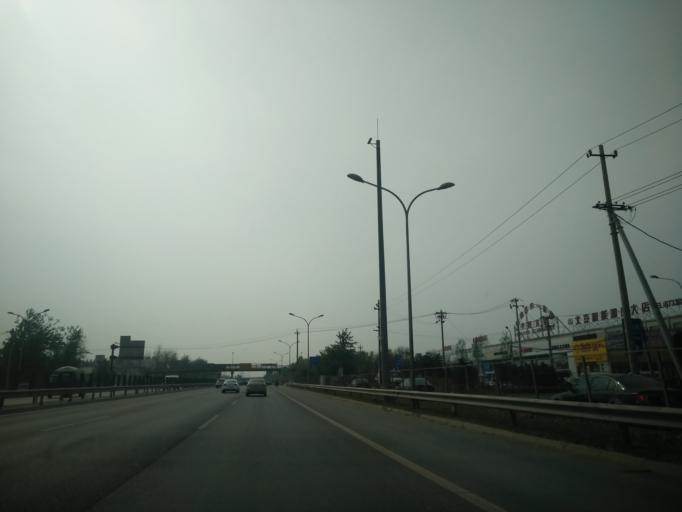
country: CN
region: Beijing
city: Dongfeng
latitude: 39.8676
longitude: 116.5530
